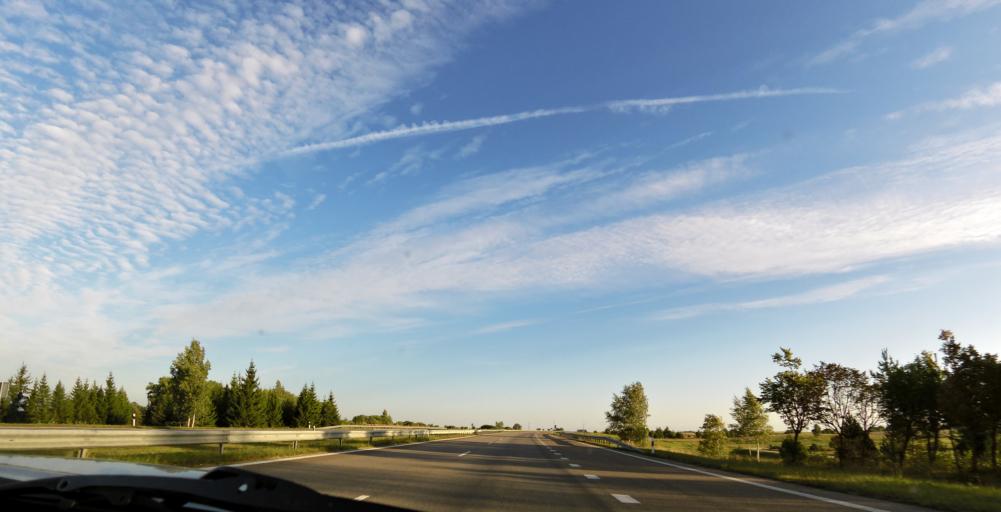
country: LT
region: Vilnius County
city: Ukmerge
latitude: 55.1797
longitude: 24.8115
